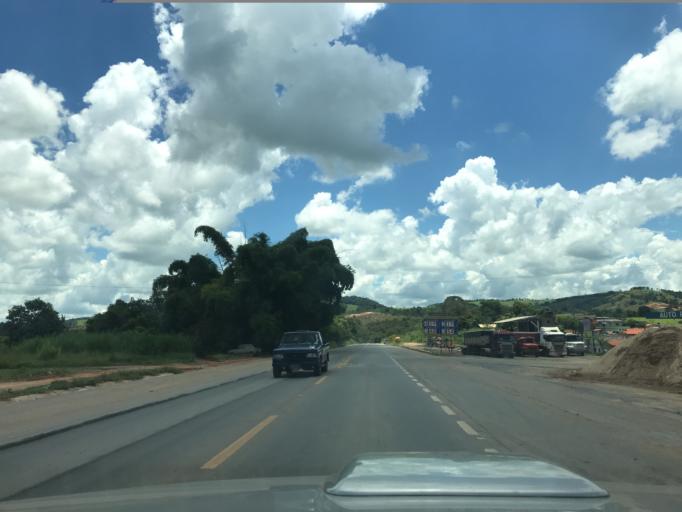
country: BR
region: Minas Gerais
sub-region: Perdoes
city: Perdoes
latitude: -21.1007
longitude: -45.0978
